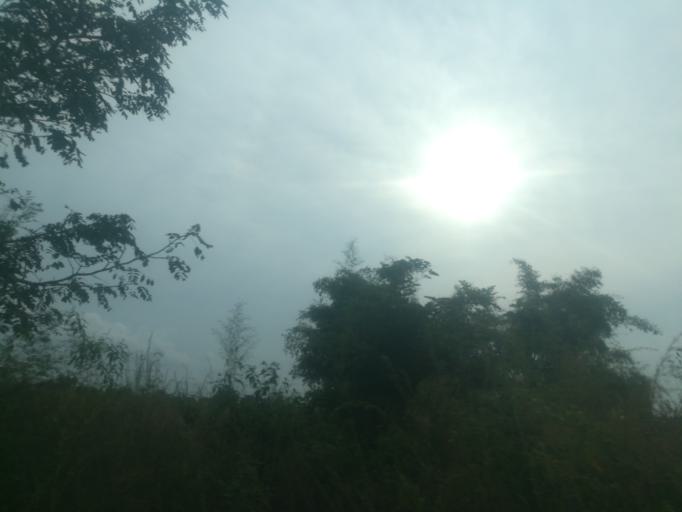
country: NG
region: Ogun
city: Ayetoro
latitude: 7.2544
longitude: 3.1152
